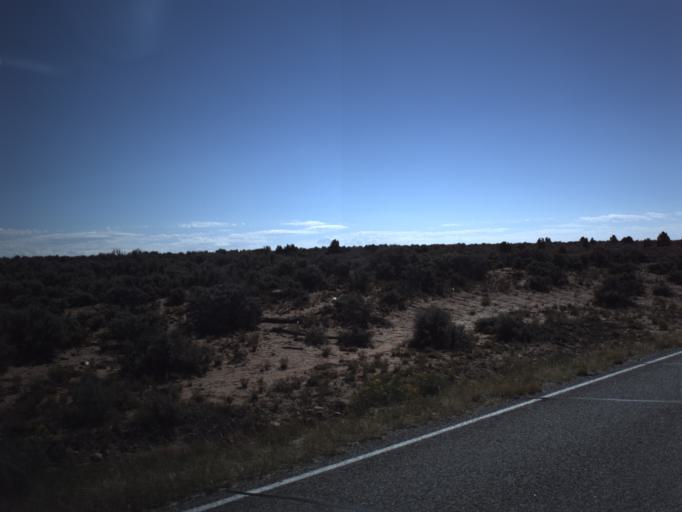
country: US
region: Utah
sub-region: San Juan County
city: Blanding
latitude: 37.5735
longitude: -109.8881
